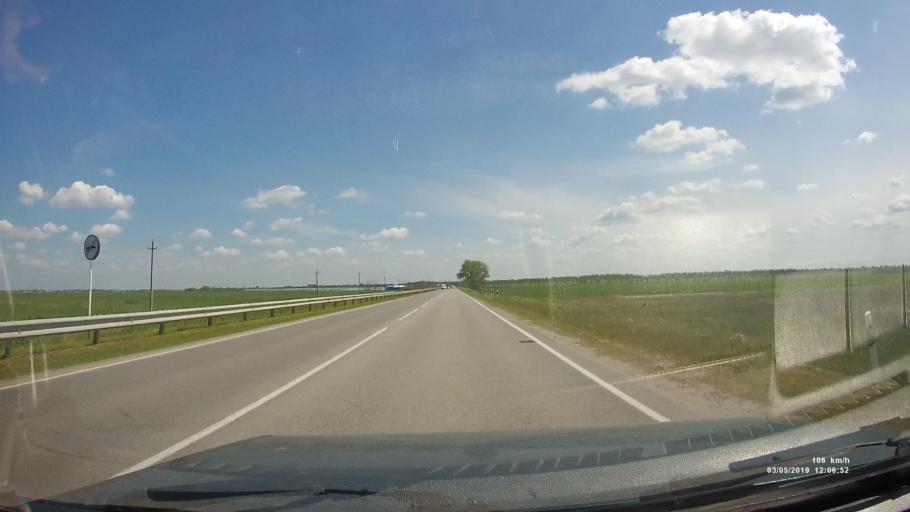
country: RU
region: Rostov
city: Bagayevskaya
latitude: 47.2853
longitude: 40.4615
